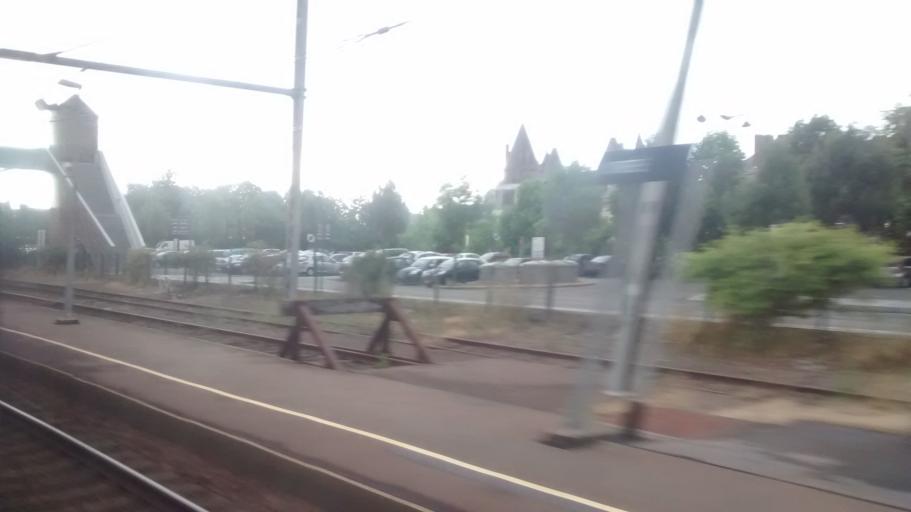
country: FR
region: Brittany
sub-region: Departement d'Ille-et-Vilaine
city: Vitre
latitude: 48.1225
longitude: -1.2123
